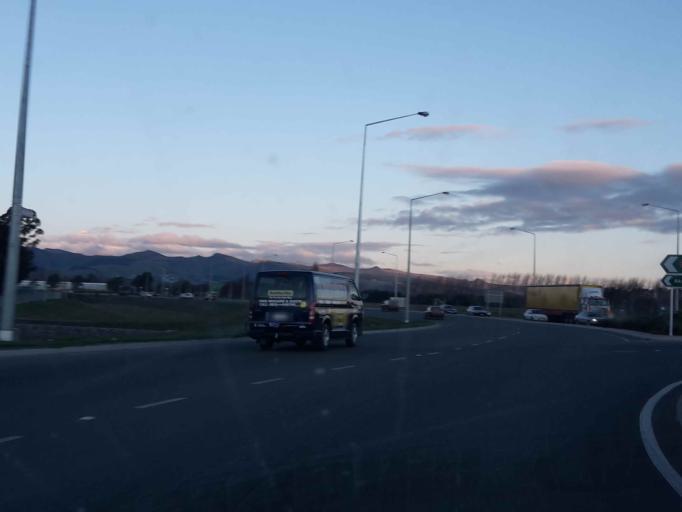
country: NZ
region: Canterbury
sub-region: Selwyn District
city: Prebbleton
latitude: -43.5614
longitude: 172.5291
